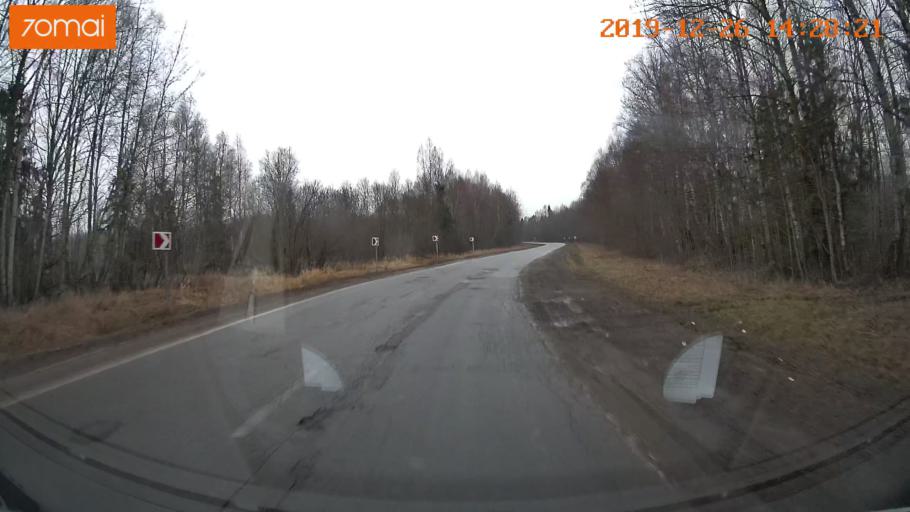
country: RU
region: Jaroslavl
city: Poshekhon'ye
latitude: 58.4762
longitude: 39.0545
